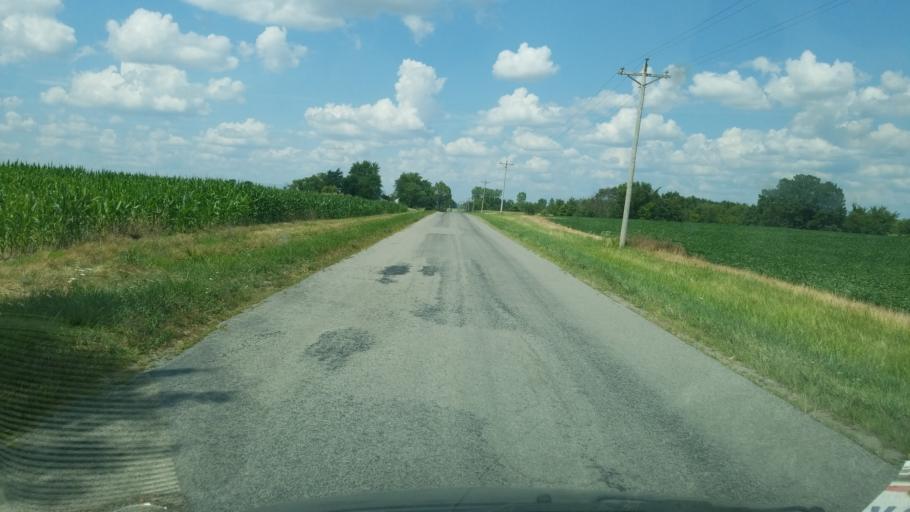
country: US
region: Ohio
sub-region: Champaign County
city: North Lewisburg
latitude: 40.3849
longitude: -83.4764
